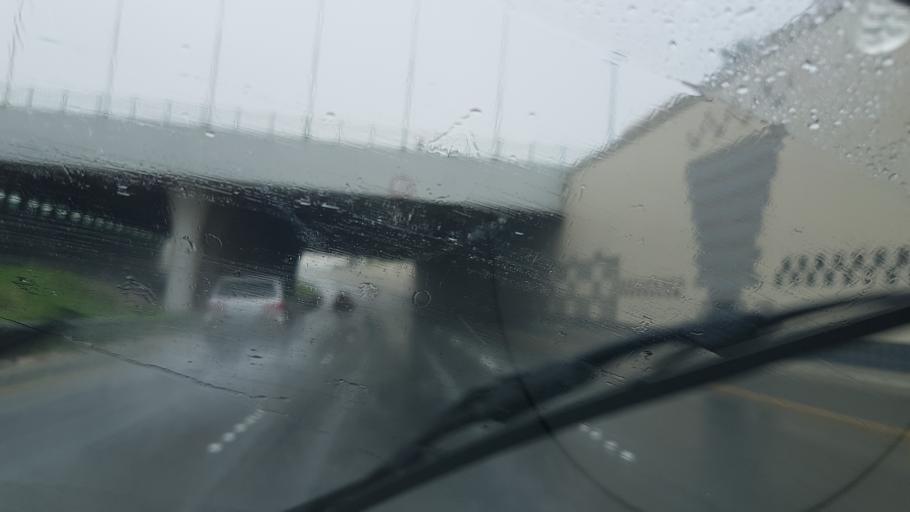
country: BH
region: Central Governorate
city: Madinat Hamad
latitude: 26.1221
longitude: 50.5069
